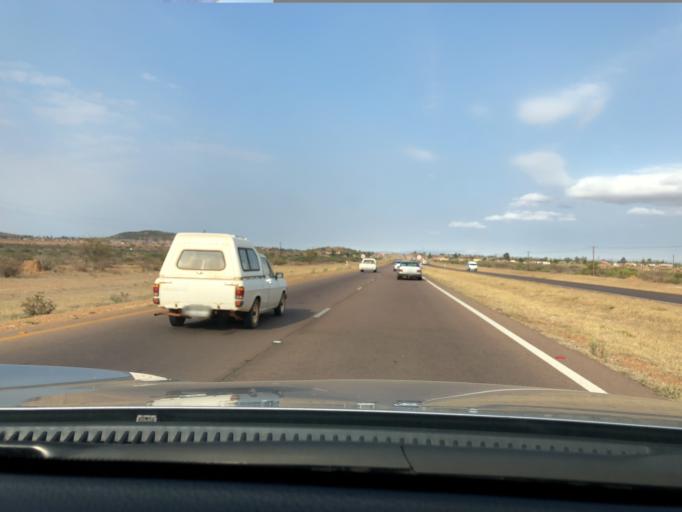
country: ZA
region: Limpopo
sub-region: Capricorn District Municipality
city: Polokwane
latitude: -23.8940
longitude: 29.6418
